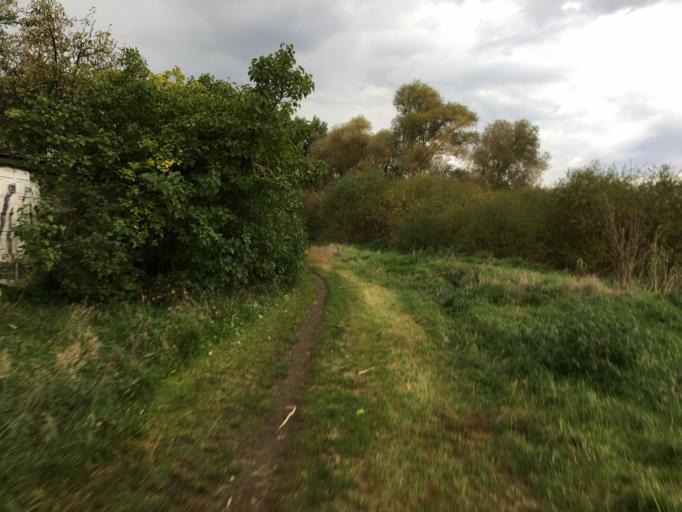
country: DE
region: Lower Saxony
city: Braunschweig
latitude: 52.2980
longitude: 10.5334
